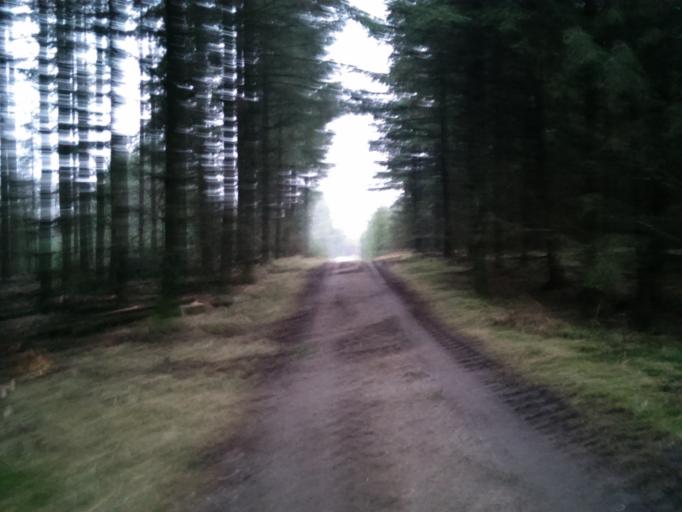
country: DK
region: North Denmark
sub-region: Mariagerfjord Kommune
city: Arden
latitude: 56.8002
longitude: 9.7572
